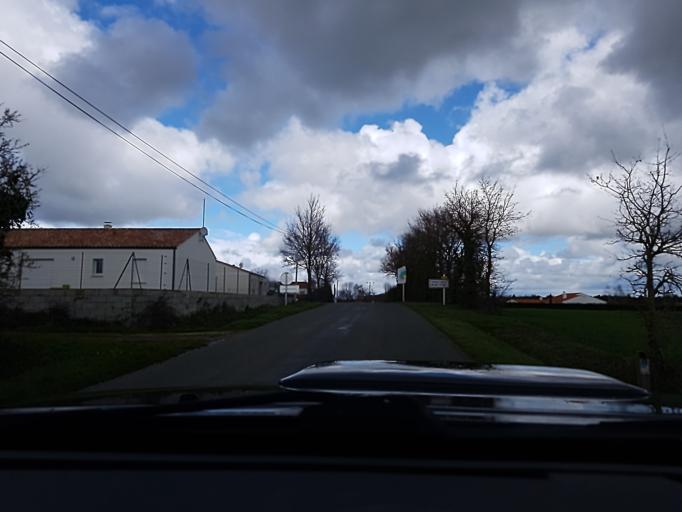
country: FR
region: Pays de la Loire
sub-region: Departement de la Vendee
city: Mache
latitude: 46.7918
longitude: -1.6628
